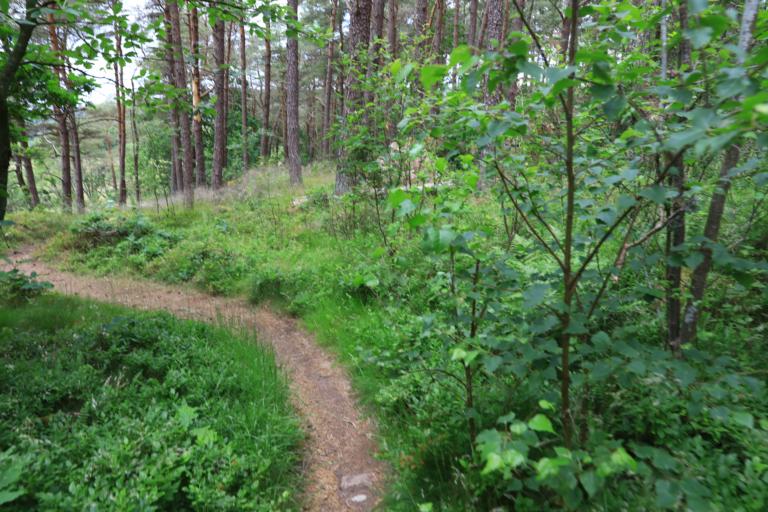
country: SE
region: Halland
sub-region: Varbergs Kommun
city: Varberg
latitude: 57.1676
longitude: 12.2485
